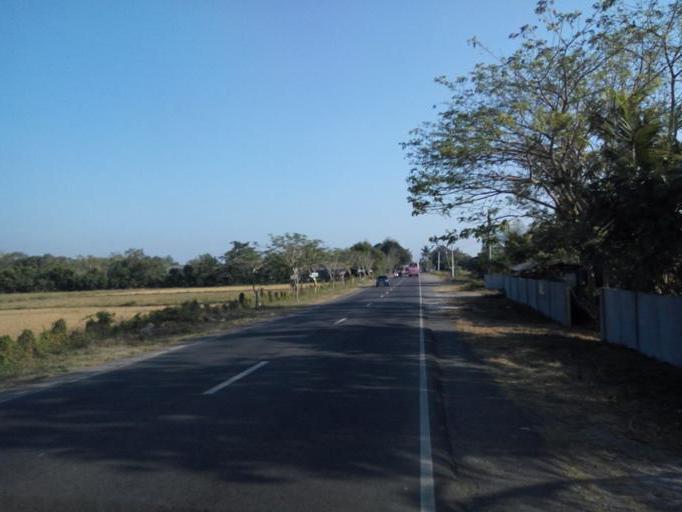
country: PH
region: Cagayan Valley
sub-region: Province of Cagayan
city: Iguig
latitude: 17.7320
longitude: 121.7386
